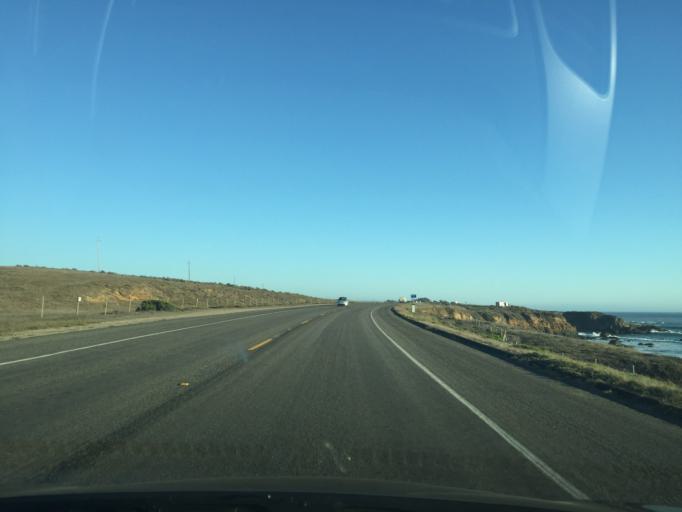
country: US
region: California
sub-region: San Luis Obispo County
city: Cambria
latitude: 35.6254
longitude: -121.1569
